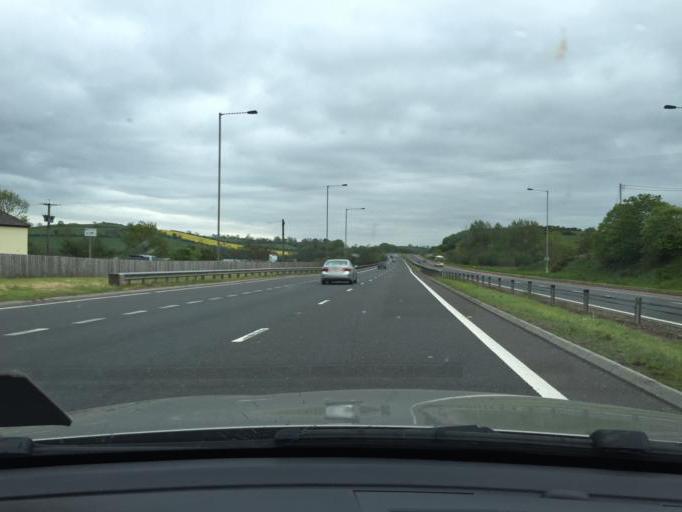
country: GB
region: Northern Ireland
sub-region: Banbridge District
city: Banbridge
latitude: 54.3112
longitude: -6.2989
